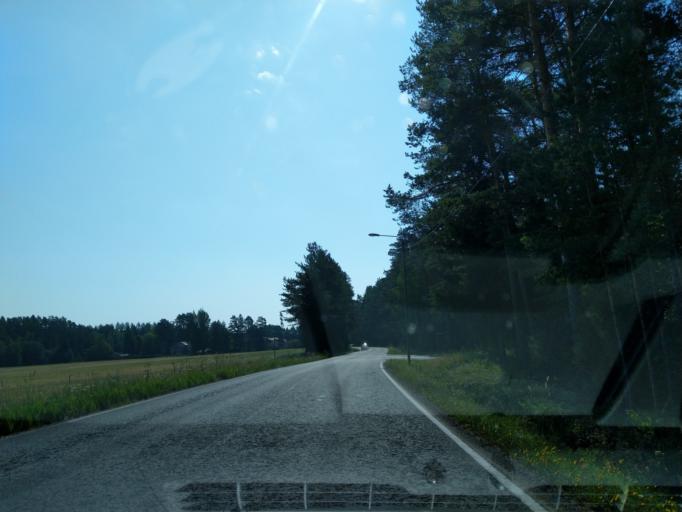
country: FI
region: Satakunta
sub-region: Pori
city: Noormarkku
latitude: 61.5860
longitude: 21.8976
